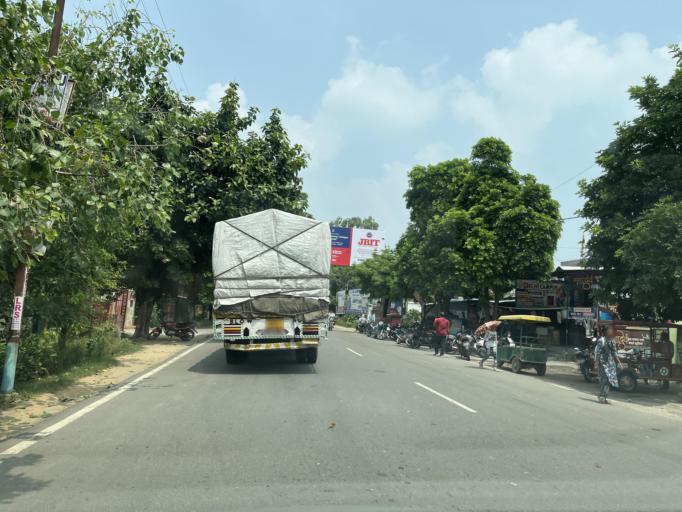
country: IN
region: Uttar Pradesh
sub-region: Bijnor
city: Najibabad
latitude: 29.5971
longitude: 78.3395
